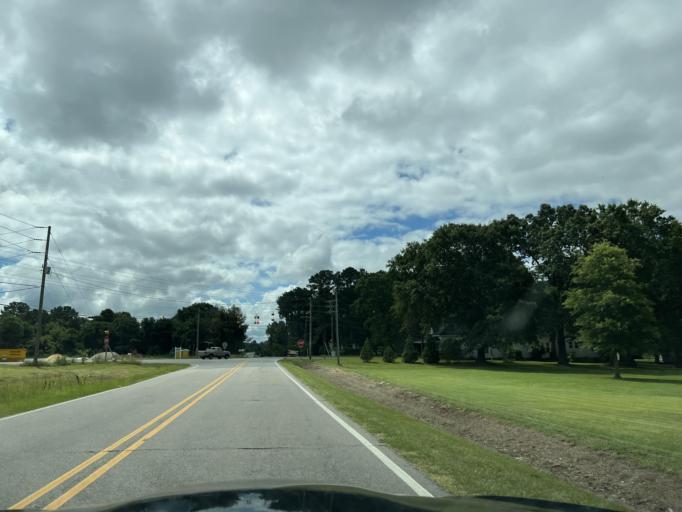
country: US
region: North Carolina
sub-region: Lee County
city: Sanford
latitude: 35.4355
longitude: -79.1671
